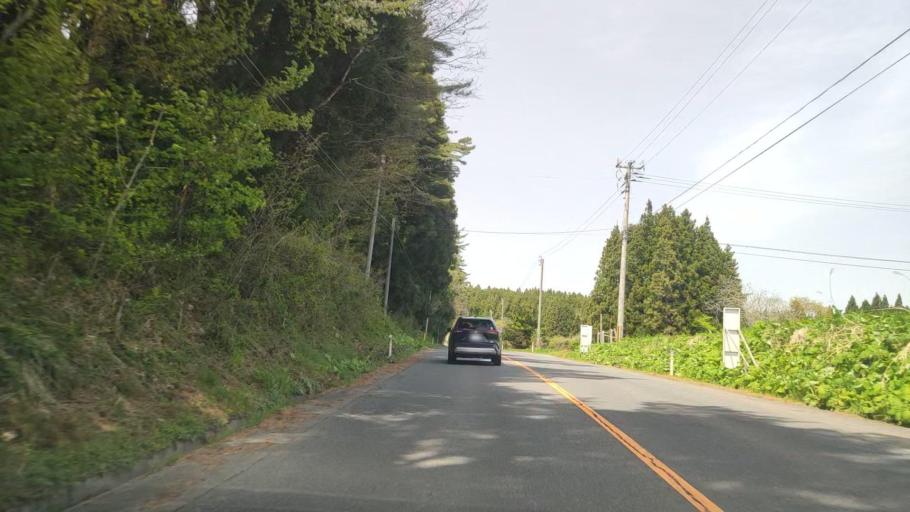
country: JP
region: Aomori
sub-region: Misawa Shi
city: Inuotose
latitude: 40.5668
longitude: 141.3797
